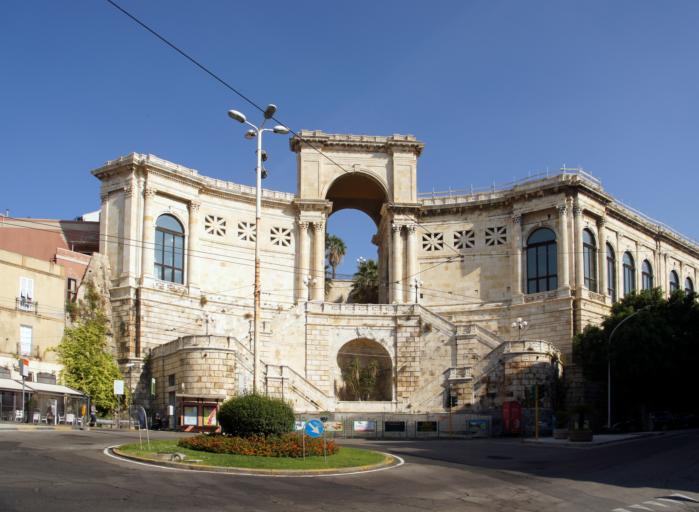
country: IT
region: Sardinia
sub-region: Provincia di Cagliari
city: Cagliari
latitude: 39.2158
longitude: 9.1160
